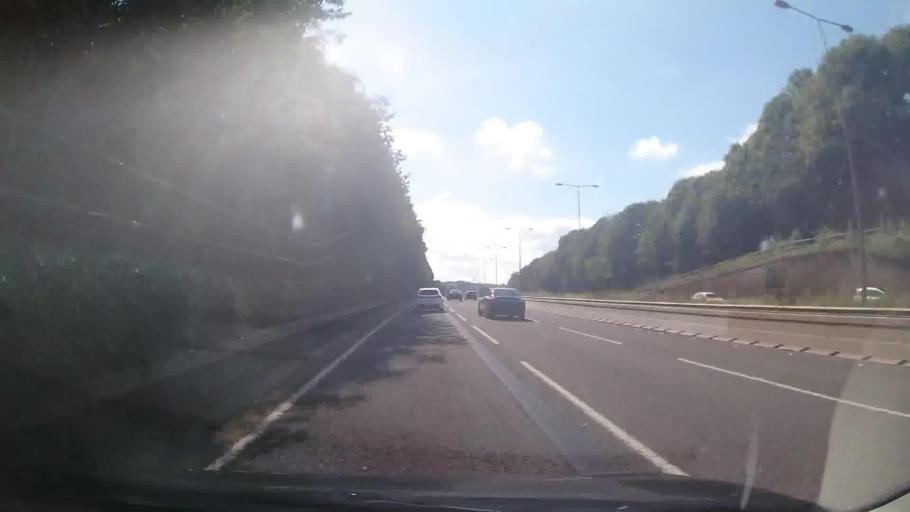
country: GB
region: England
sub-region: Borough of Wigan
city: Shevington
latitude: 53.5384
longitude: -2.6970
